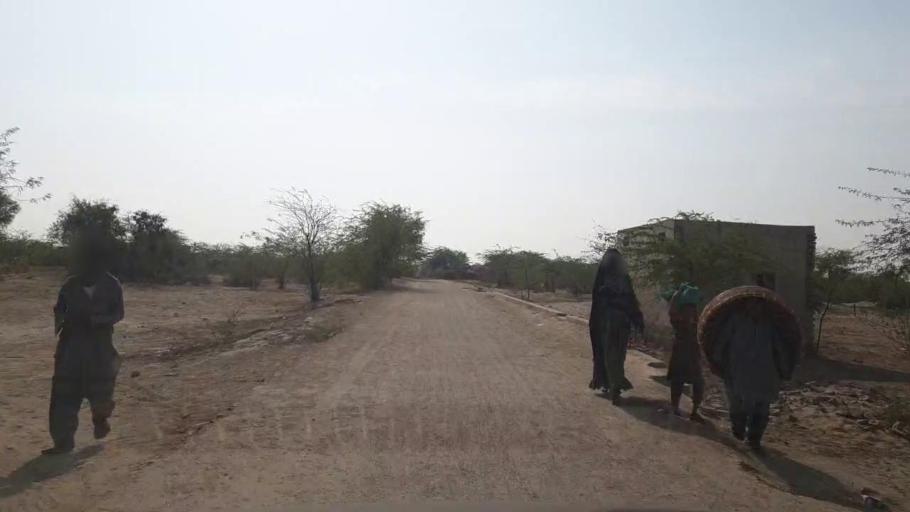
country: PK
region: Sindh
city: Umarkot
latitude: 25.3348
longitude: 69.7379
